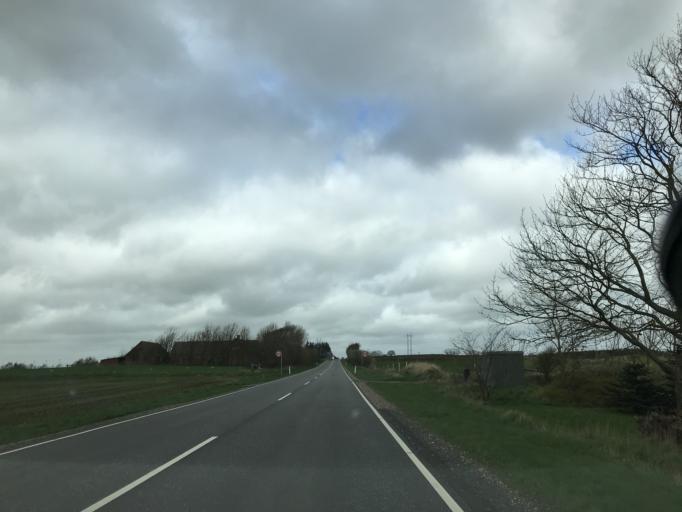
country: DK
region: Central Jutland
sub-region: Skive Kommune
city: Skive
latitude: 56.5416
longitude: 8.9819
